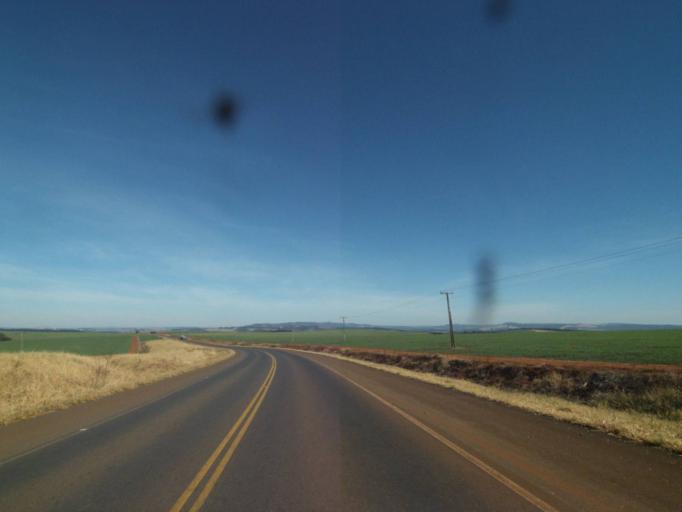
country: BR
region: Parana
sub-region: Tibagi
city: Tibagi
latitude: -24.4391
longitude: -50.4227
